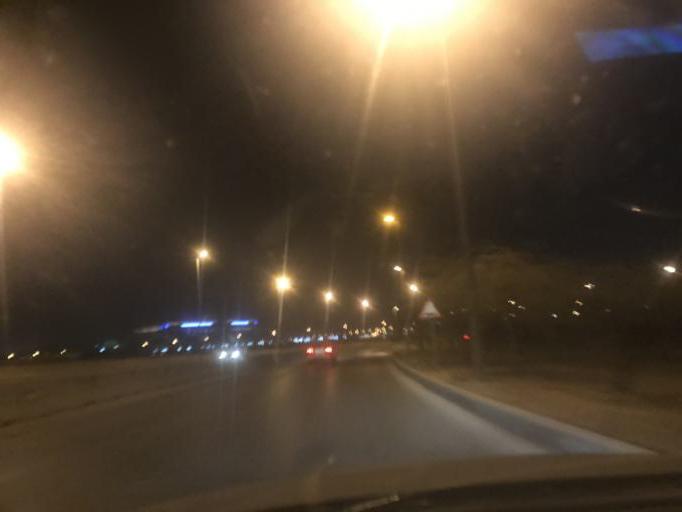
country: SA
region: Ar Riyad
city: Riyadh
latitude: 24.8282
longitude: 46.7176
